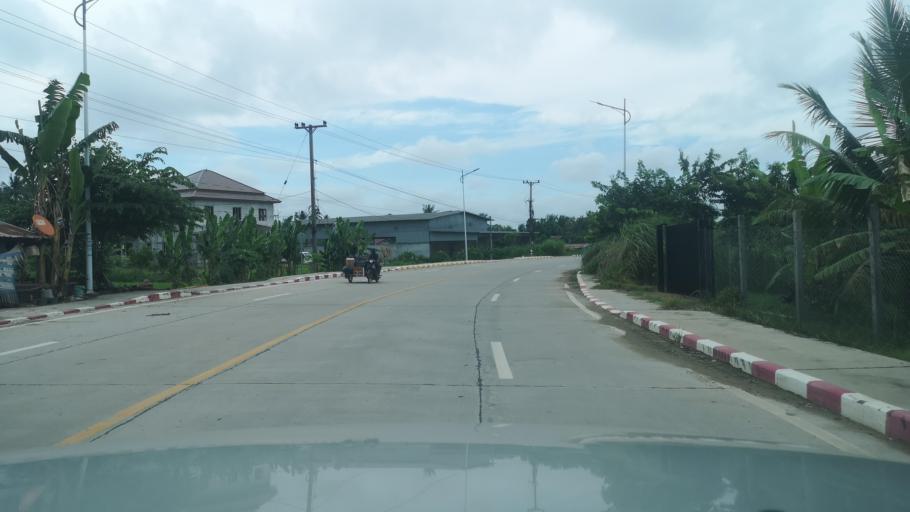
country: TH
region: Nong Khai
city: Tha Bo
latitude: 17.8215
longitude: 102.6636
